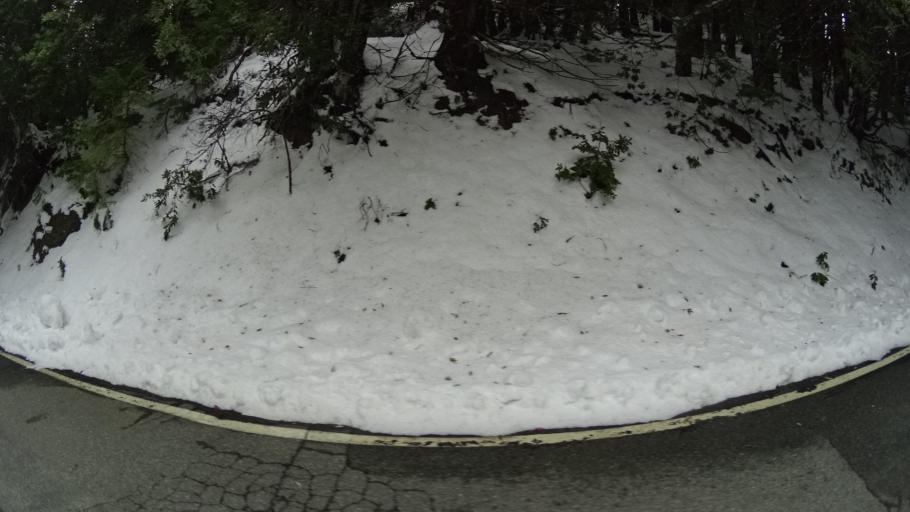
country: US
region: California
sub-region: Humboldt County
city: Willow Creek
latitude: 40.8645
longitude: -123.7417
